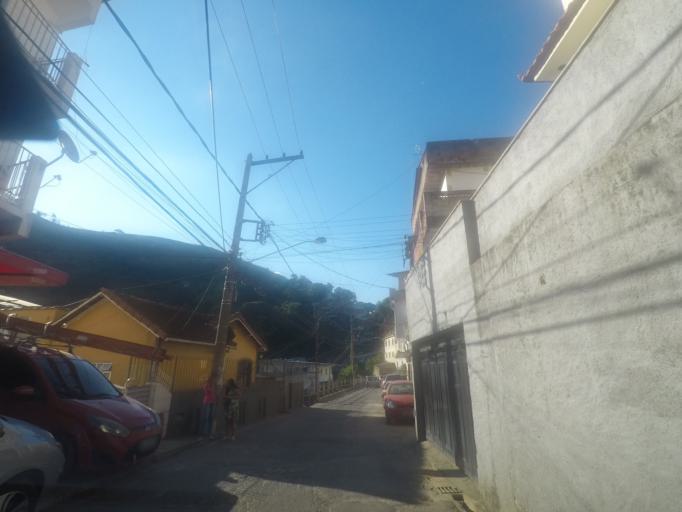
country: BR
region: Rio de Janeiro
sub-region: Petropolis
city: Petropolis
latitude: -22.4972
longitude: -43.1489
